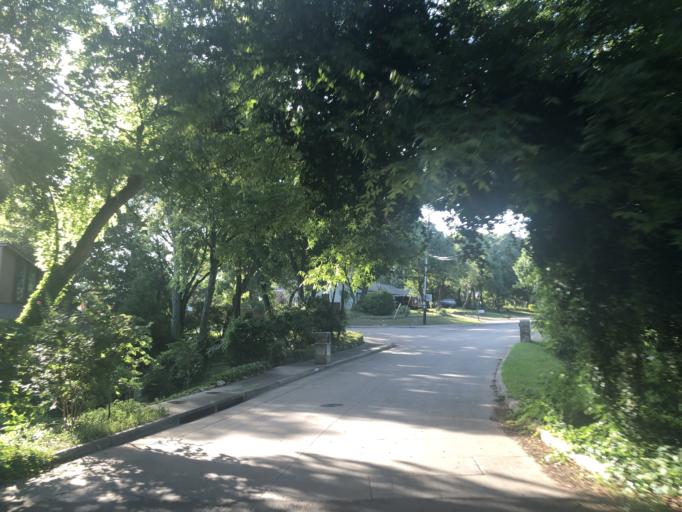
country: US
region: Texas
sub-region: Dallas County
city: Duncanville
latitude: 32.6719
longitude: -96.9136
